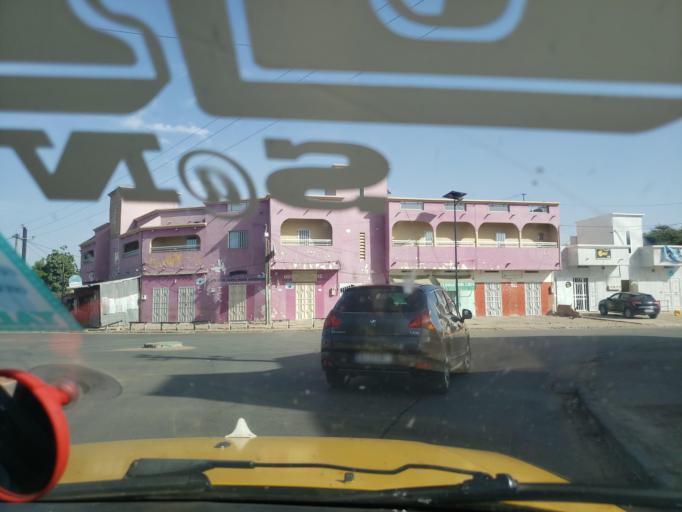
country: SN
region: Louga
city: Louga
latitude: 15.6220
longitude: -16.2105
